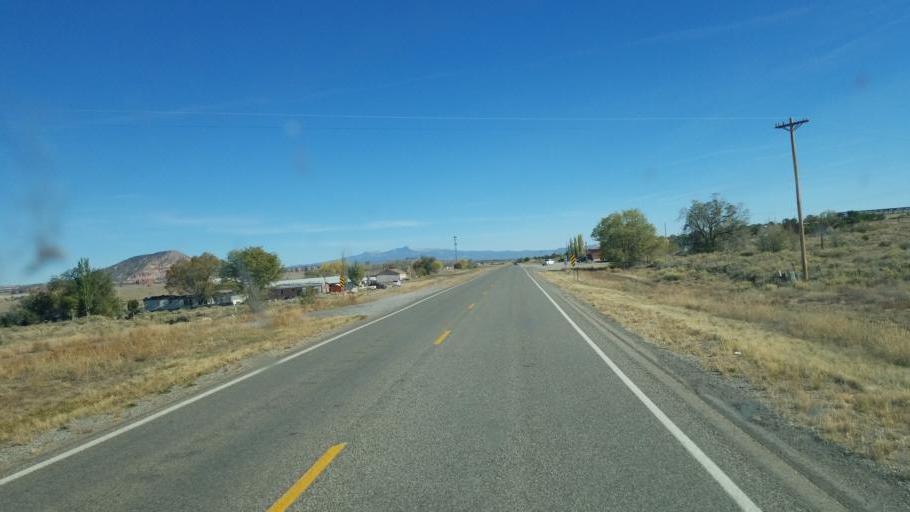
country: US
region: New Mexico
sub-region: McKinley County
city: Thoreau
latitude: 35.3579
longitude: -108.0275
